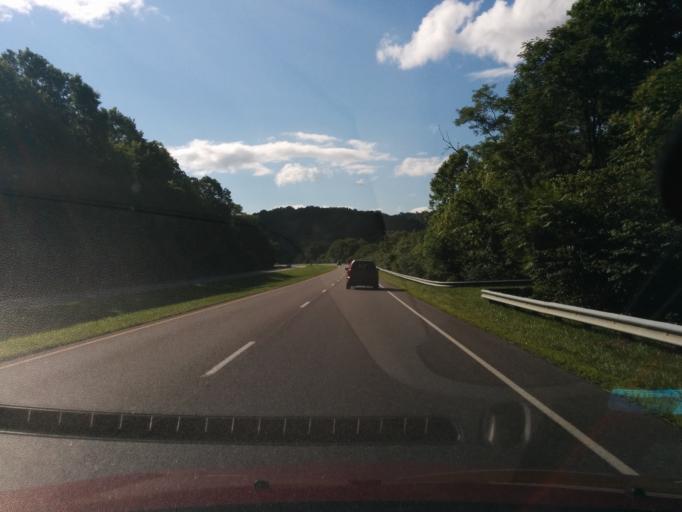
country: US
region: Virginia
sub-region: City of Lexington
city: Lexington
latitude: 37.7622
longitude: -79.4256
